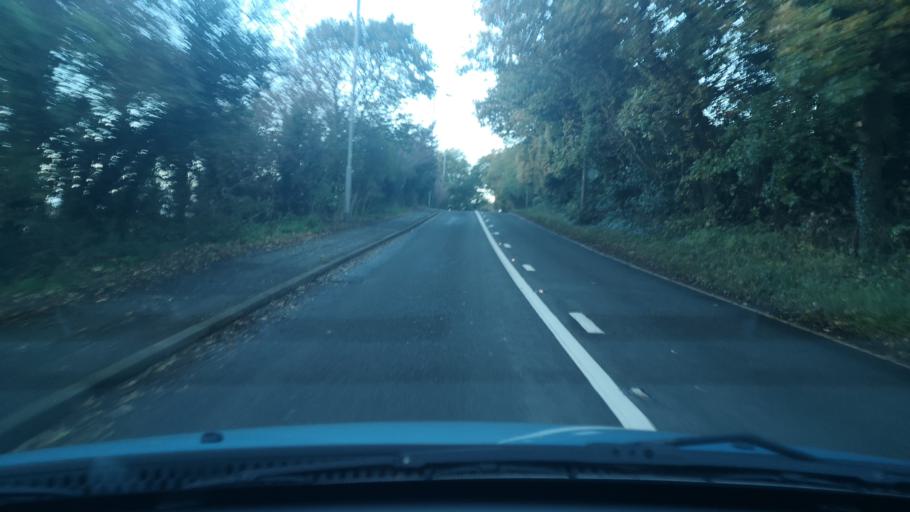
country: GB
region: England
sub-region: City and Borough of Wakefield
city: Middlestown
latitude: 53.6341
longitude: -1.5867
